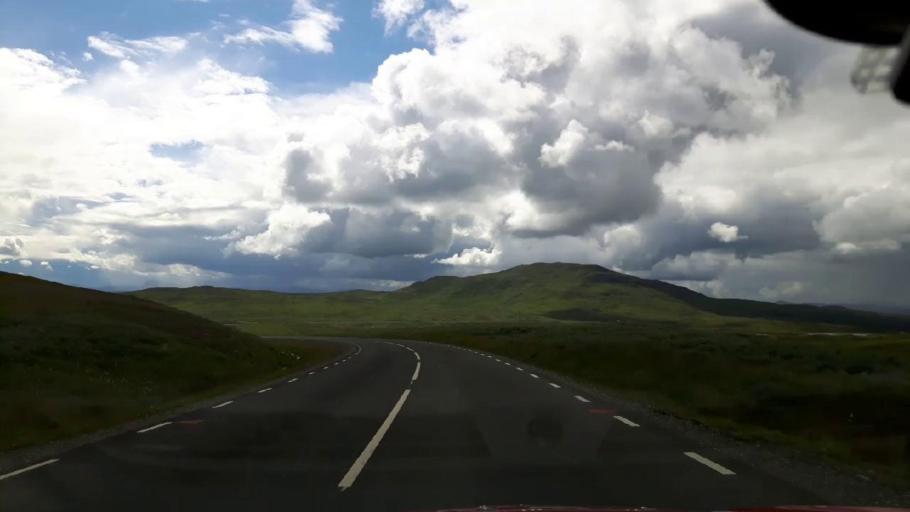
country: NO
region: Nordland
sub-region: Hattfjelldal
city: Hattfjelldal
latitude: 65.0390
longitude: 14.3269
